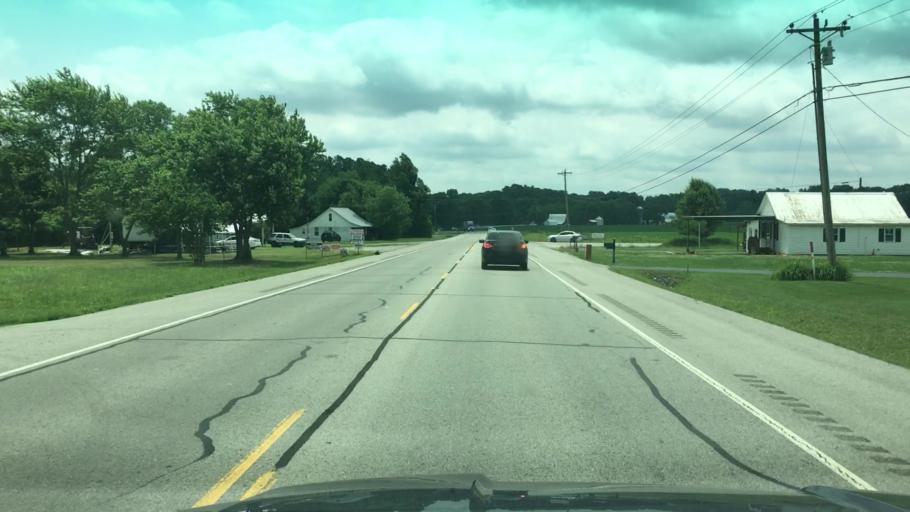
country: US
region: Tennessee
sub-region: Coffee County
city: New Union
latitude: 35.5291
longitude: -86.1590
